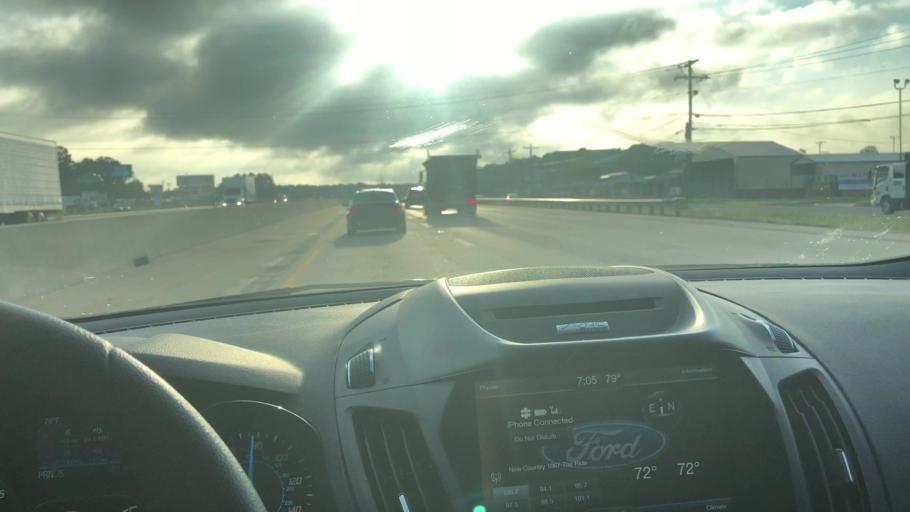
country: US
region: Arkansas
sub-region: Pulaski County
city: Alexander
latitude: 34.6411
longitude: -92.4436
